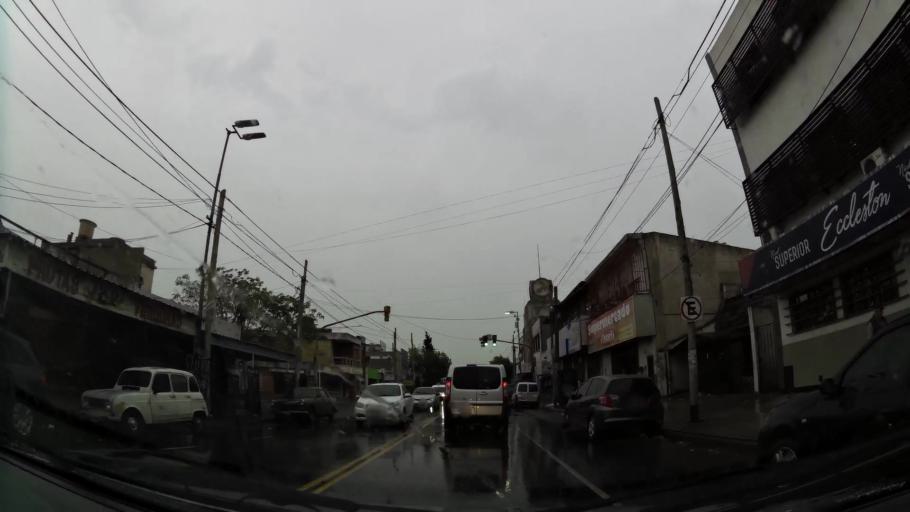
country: AR
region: Buenos Aires
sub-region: Partido de Lanus
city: Lanus
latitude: -34.7062
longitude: -58.4035
